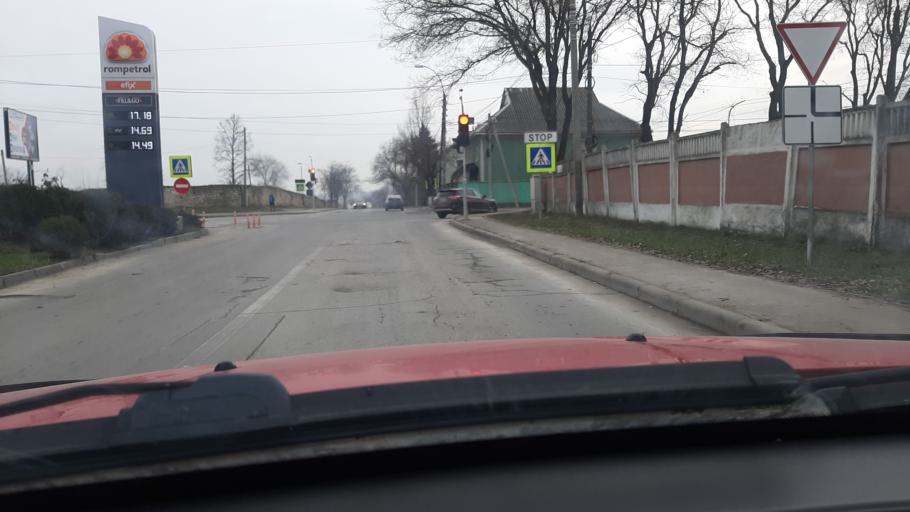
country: MD
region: Chisinau
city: Vatra
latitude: 47.0353
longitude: 28.7940
